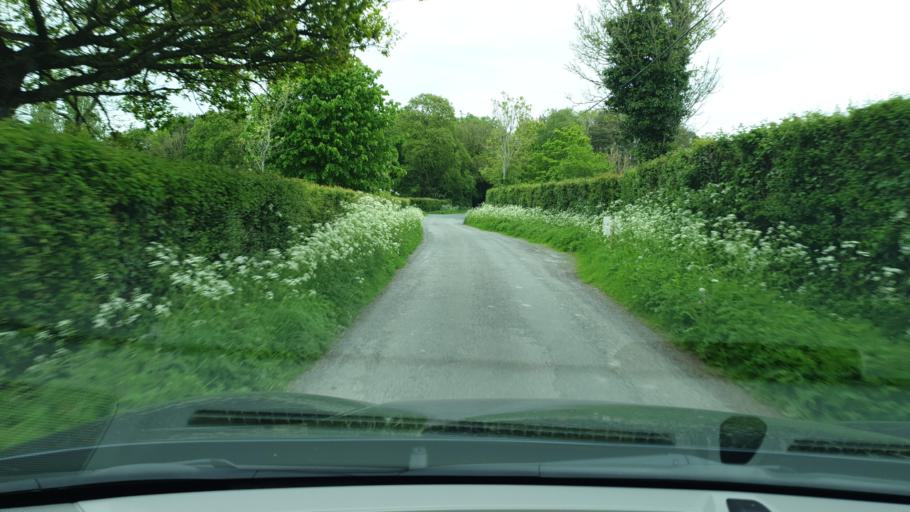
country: IE
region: Leinster
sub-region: An Mhi
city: Dunboyne
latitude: 53.4451
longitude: -6.5204
